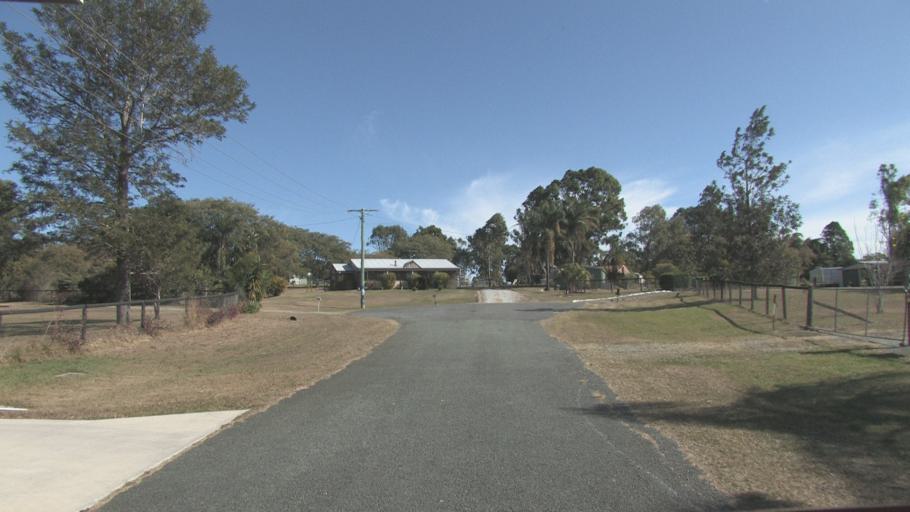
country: AU
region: Queensland
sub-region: Logan
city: Cedar Vale
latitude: -27.8565
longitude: 152.9755
